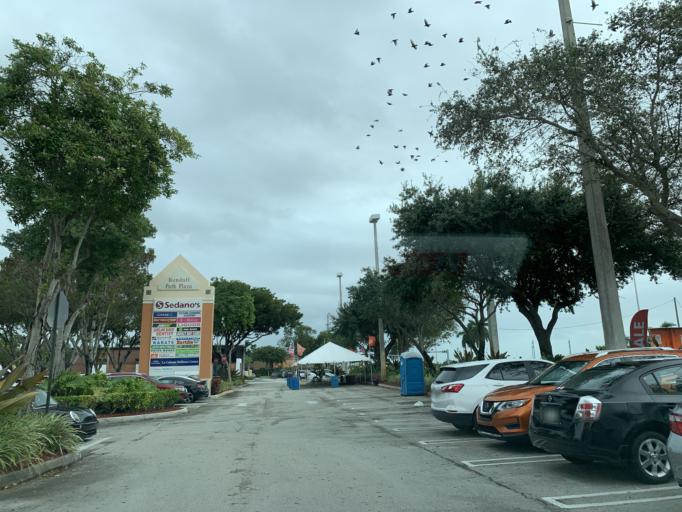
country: US
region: Florida
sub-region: Miami-Dade County
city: The Hammocks
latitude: 25.6844
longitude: -80.4557
